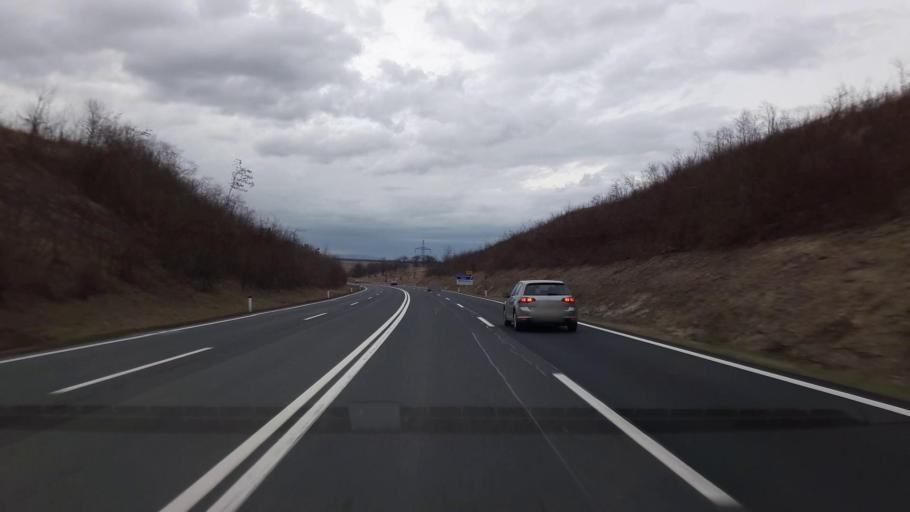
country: AT
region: Burgenland
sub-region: Politischer Bezirk Mattersburg
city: Mattersburg
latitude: 47.7136
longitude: 16.3867
